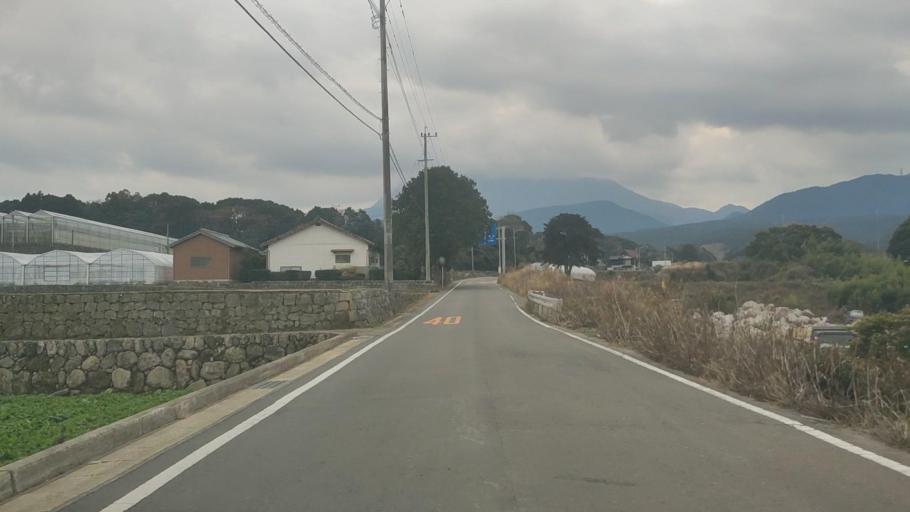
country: JP
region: Nagasaki
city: Shimabara
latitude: 32.8287
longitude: 130.2919
